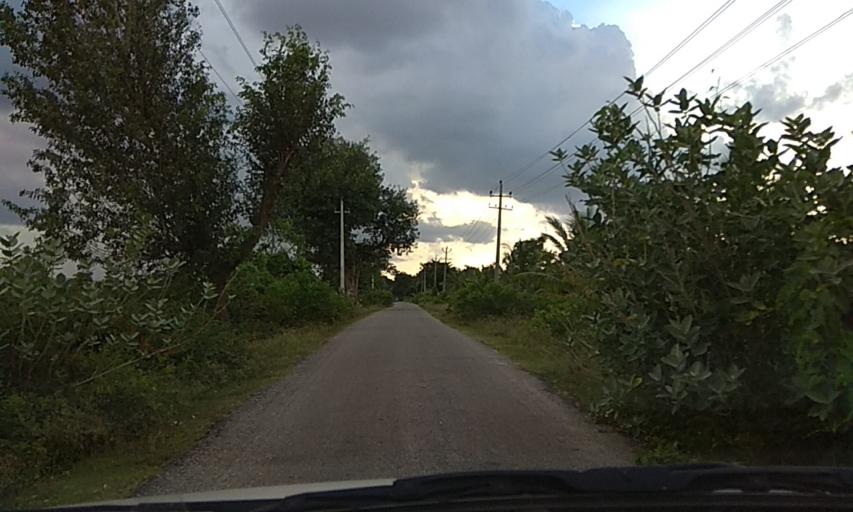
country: IN
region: Karnataka
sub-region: Chamrajnagar
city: Gundlupet
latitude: 11.8712
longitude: 76.7461
